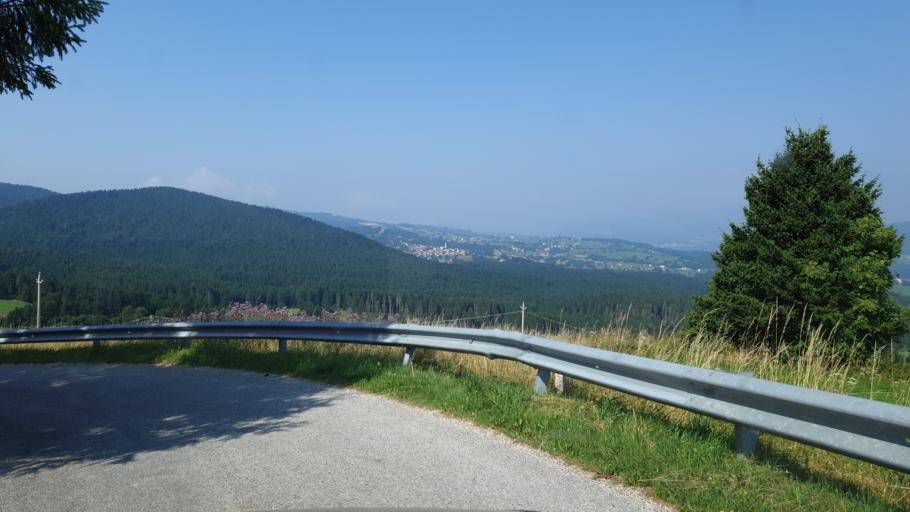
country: IT
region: Veneto
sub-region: Provincia di Vicenza
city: Canove di Roana
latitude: 45.8457
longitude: 11.4962
